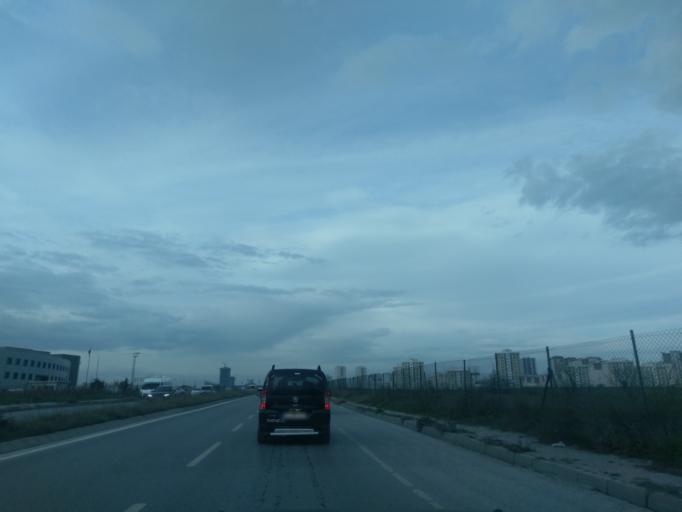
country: TR
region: Istanbul
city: Esenyurt
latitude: 41.0777
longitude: 28.6545
